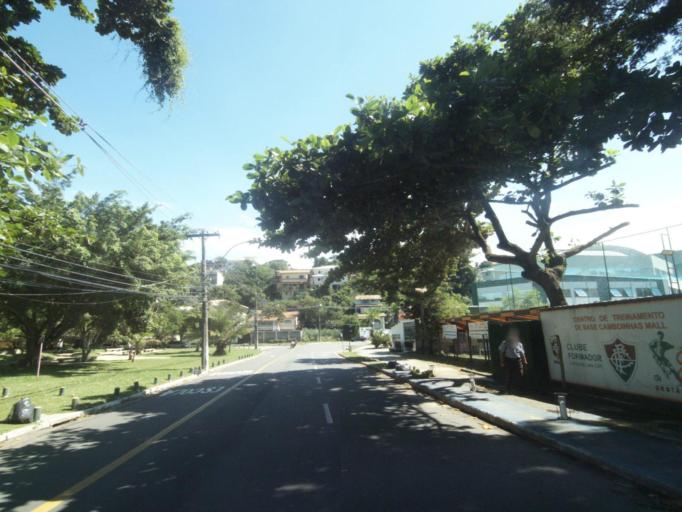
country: BR
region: Rio de Janeiro
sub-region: Niteroi
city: Niteroi
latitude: -22.9531
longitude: -43.0590
